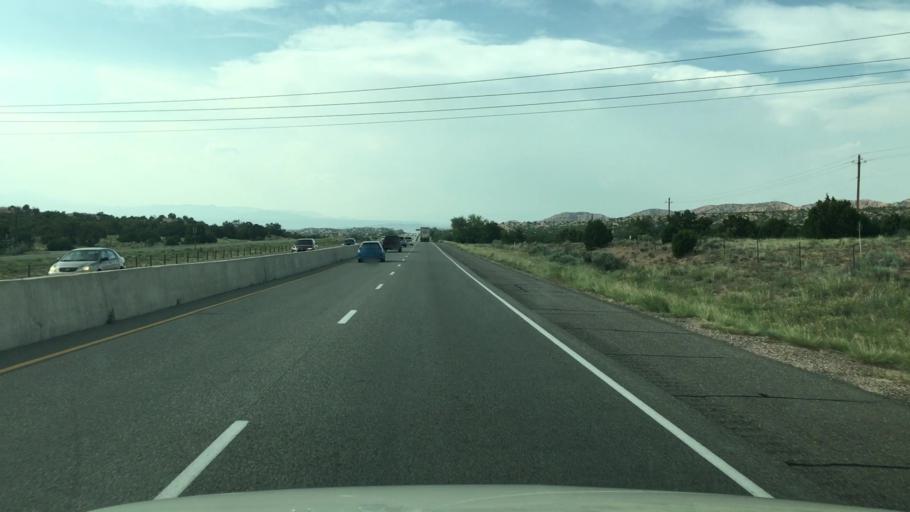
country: US
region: New Mexico
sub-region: Santa Fe County
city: Nambe
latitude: 35.7932
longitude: -105.9543
